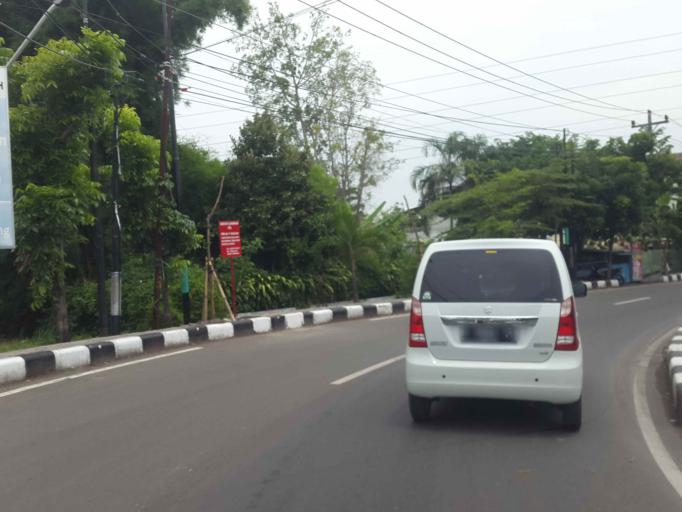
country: ID
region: Central Java
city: Semarang
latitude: -7.0226
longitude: 110.4628
